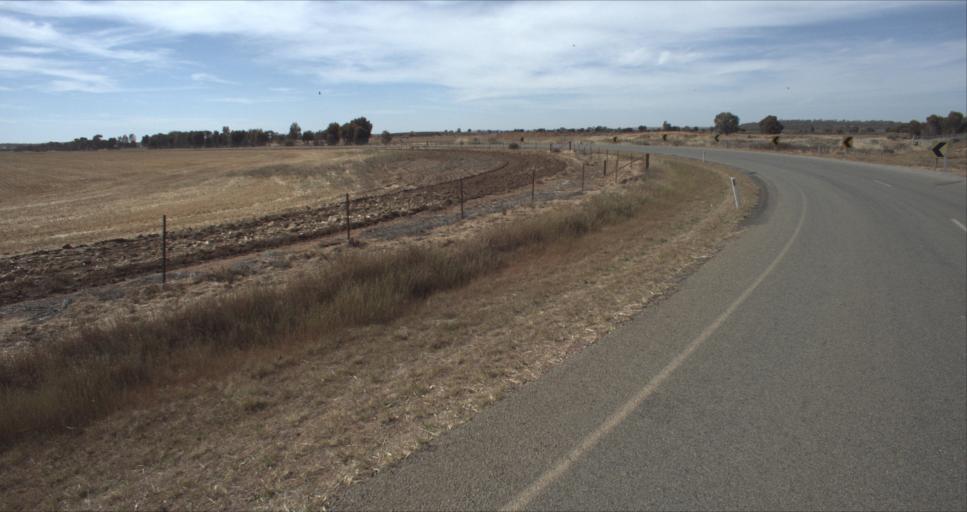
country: AU
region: New South Wales
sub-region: Leeton
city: Leeton
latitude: -34.5630
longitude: 146.4814
